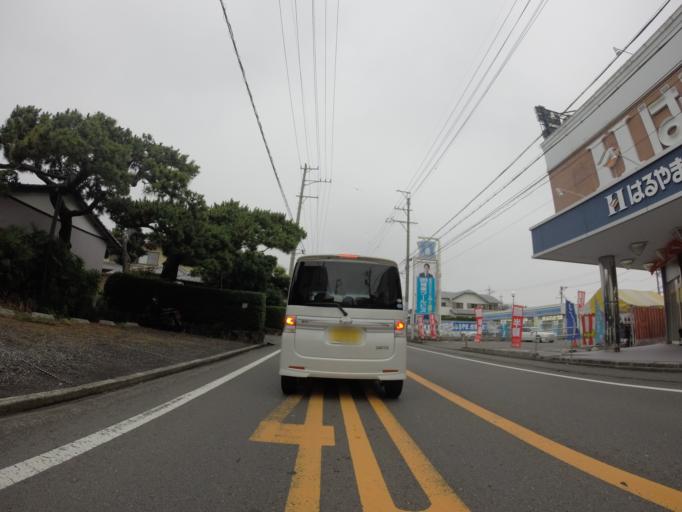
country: JP
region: Shizuoka
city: Shizuoka-shi
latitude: 34.9524
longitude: 138.3951
